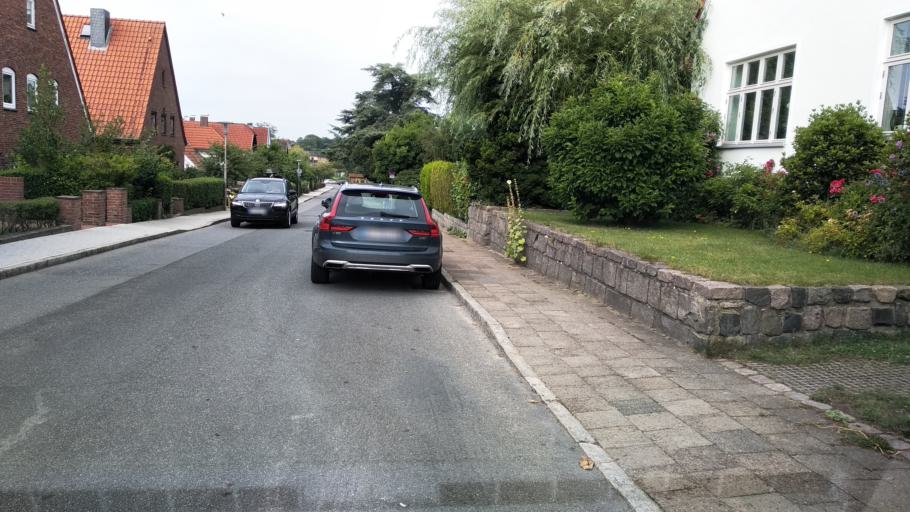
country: DE
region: Schleswig-Holstein
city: Schleswig
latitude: 54.5180
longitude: 9.5769
